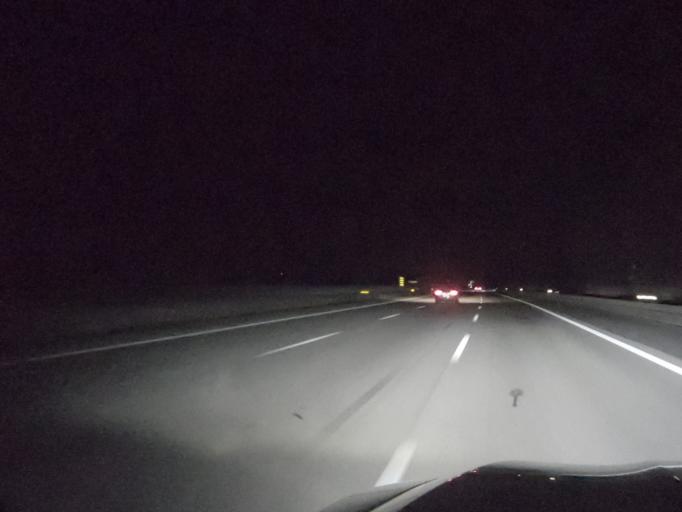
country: PT
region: Lisbon
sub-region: Alenquer
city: Carregado
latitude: 39.0438
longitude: -8.9504
